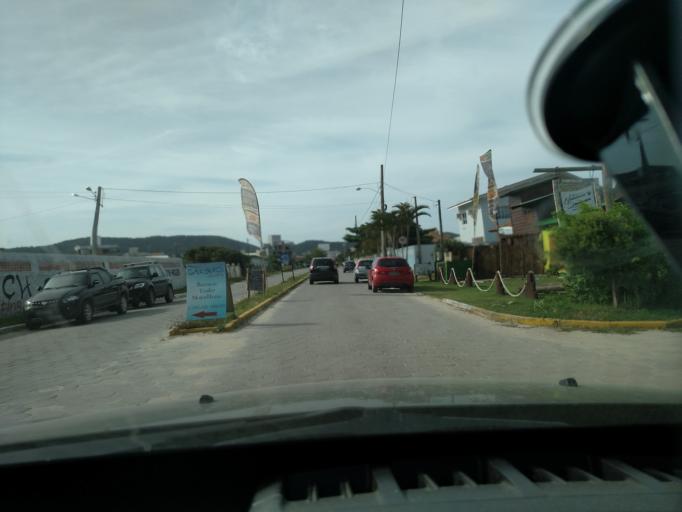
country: BR
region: Santa Catarina
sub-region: Porto Belo
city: Porto Belo
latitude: -27.1888
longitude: -48.4998
